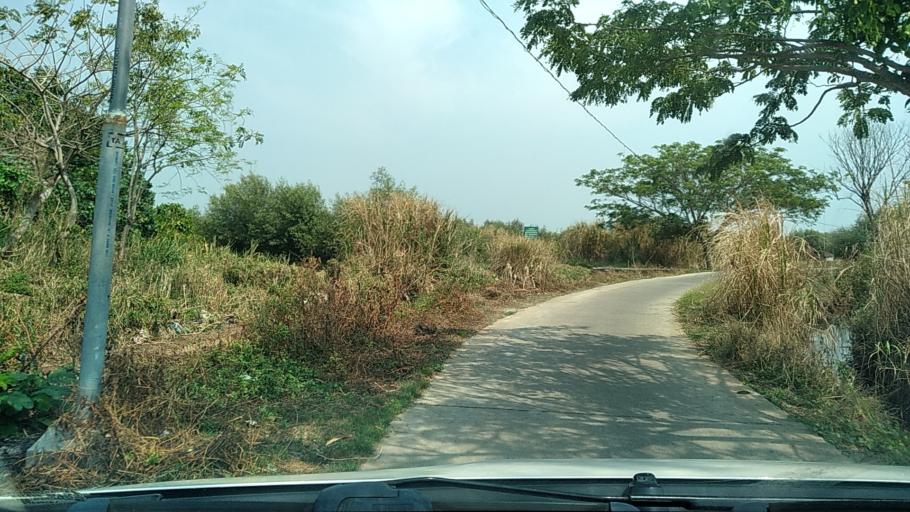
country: ID
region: Central Java
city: Semarang
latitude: -6.9679
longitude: 110.3457
